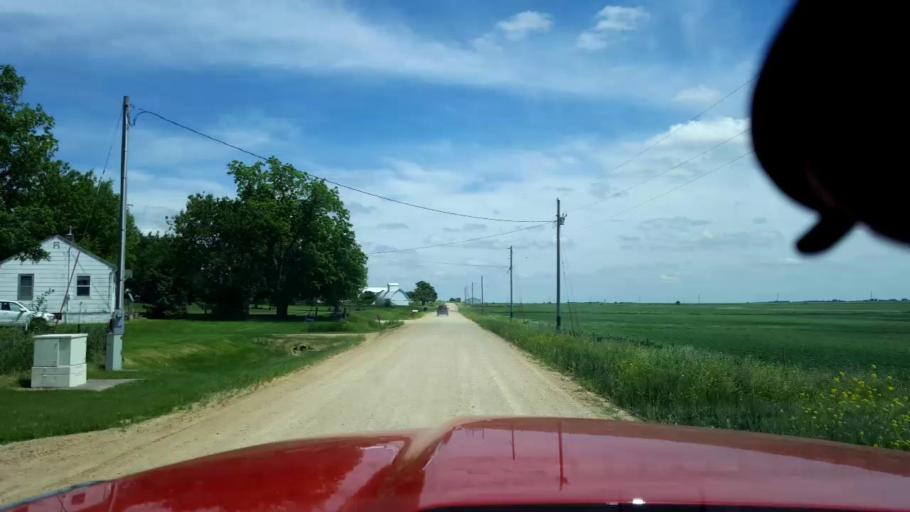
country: US
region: Iowa
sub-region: Linn County
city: Lisbon
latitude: 41.9535
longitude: -91.3586
